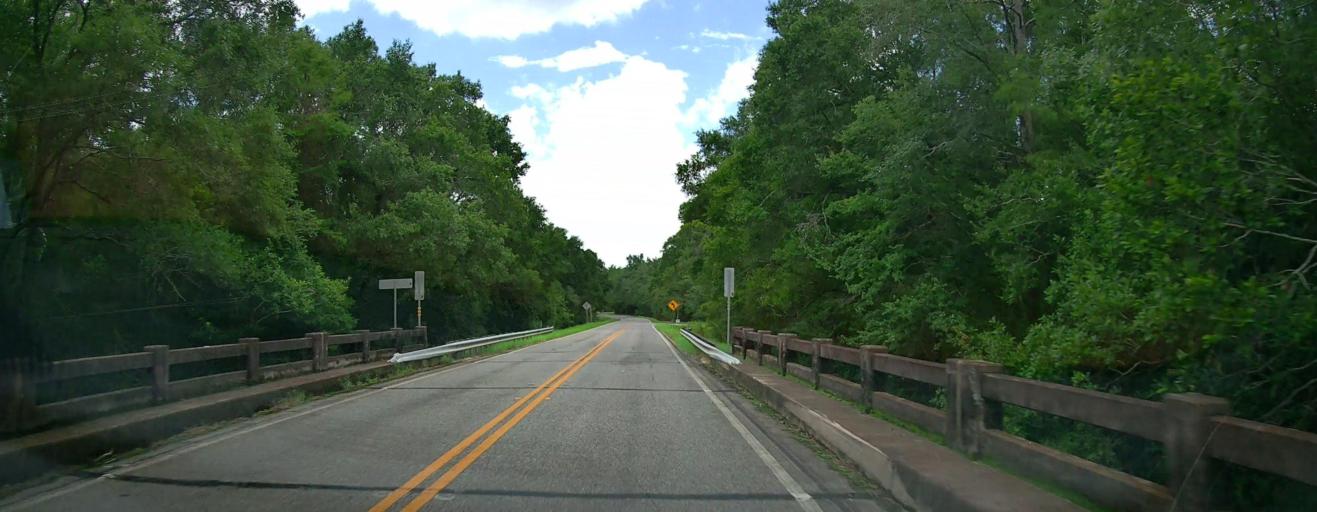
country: US
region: Georgia
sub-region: Wilcox County
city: Rochelle
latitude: 31.9307
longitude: -83.5520
